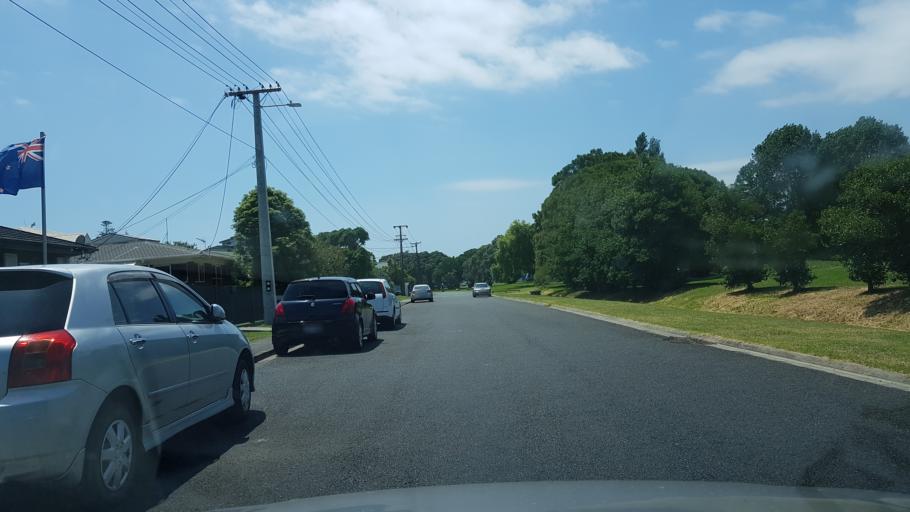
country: NZ
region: Auckland
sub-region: Auckland
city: North Shore
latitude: -36.8150
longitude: 174.7983
